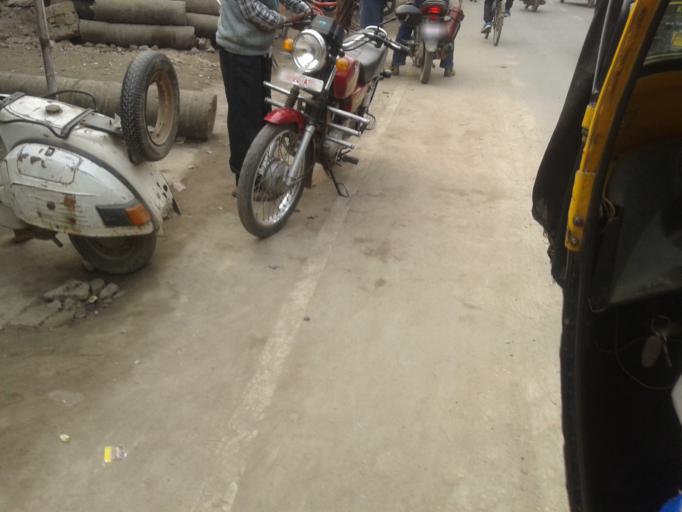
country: IN
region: Bihar
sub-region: Muzaffarpur
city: Muzaffarpur
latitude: 26.1152
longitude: 85.3808
